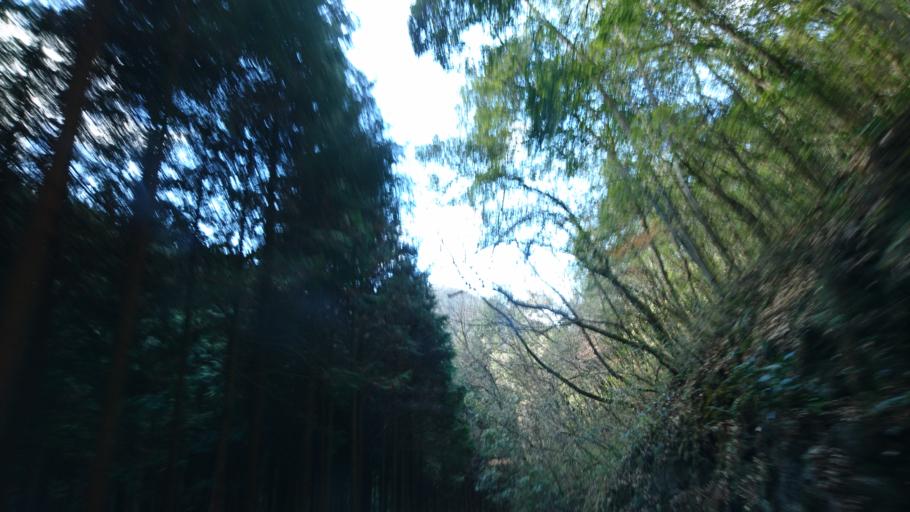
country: JP
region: Okayama
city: Takahashi
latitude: 34.8638
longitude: 133.5672
